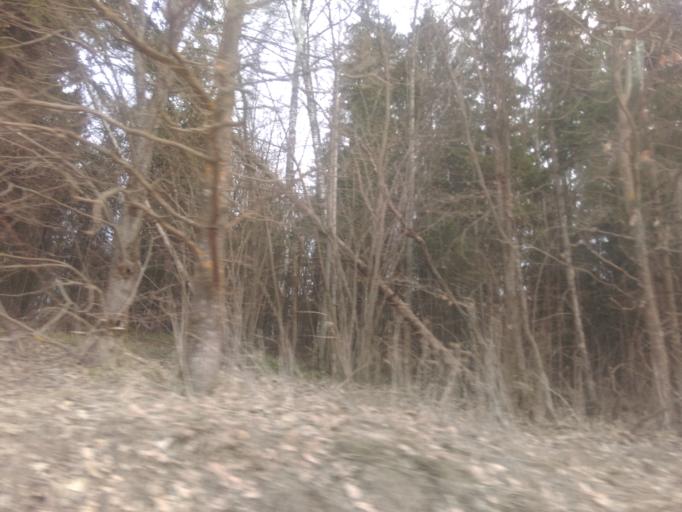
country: RU
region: Moskovskaya
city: Tuchkovo
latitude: 55.6141
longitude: 36.4223
